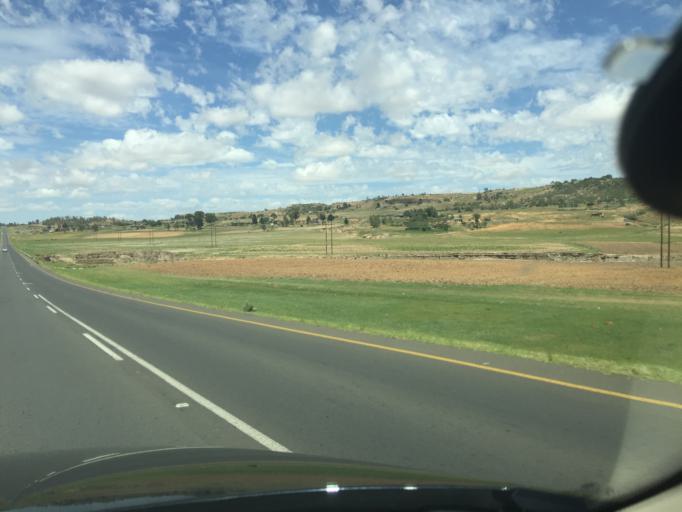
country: LS
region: Mafeteng
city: Mafeteng
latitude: -29.7622
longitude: 27.3226
